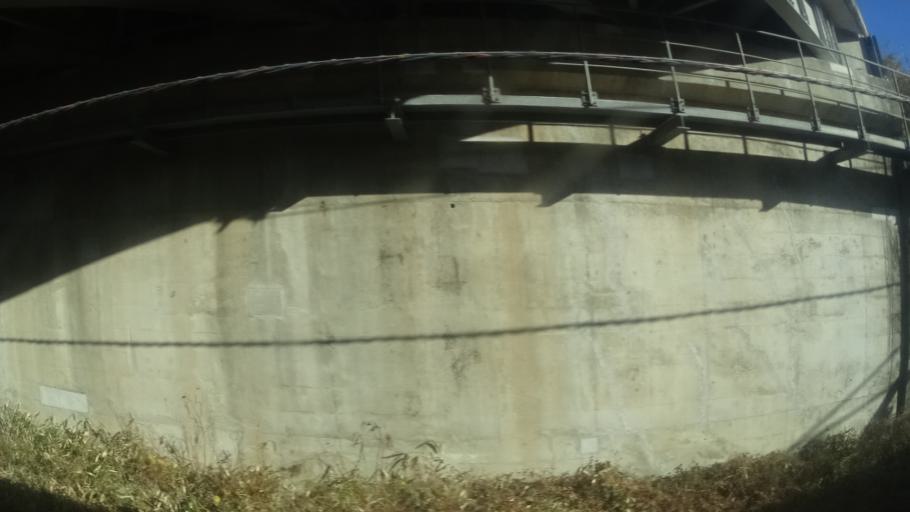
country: JP
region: Miyagi
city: Marumori
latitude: 37.8112
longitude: 140.9231
